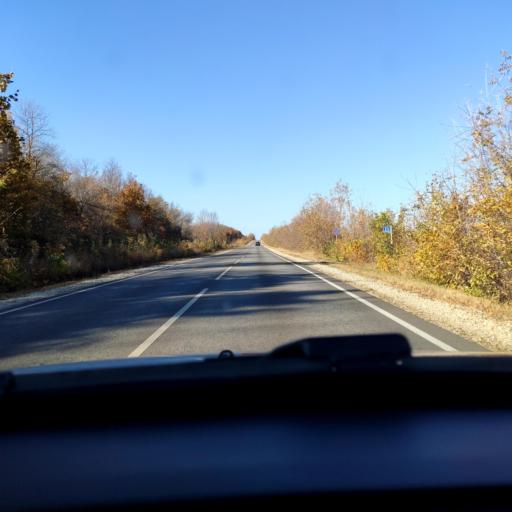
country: RU
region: Voronezj
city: Zemlyansk
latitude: 51.8524
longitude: 38.7953
